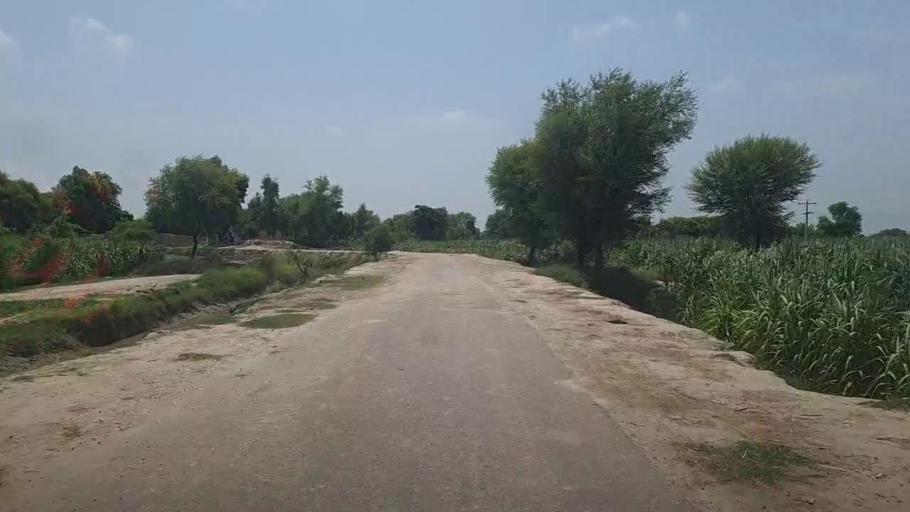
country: PK
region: Sindh
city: Ubauro
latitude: 28.2799
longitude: 69.8085
